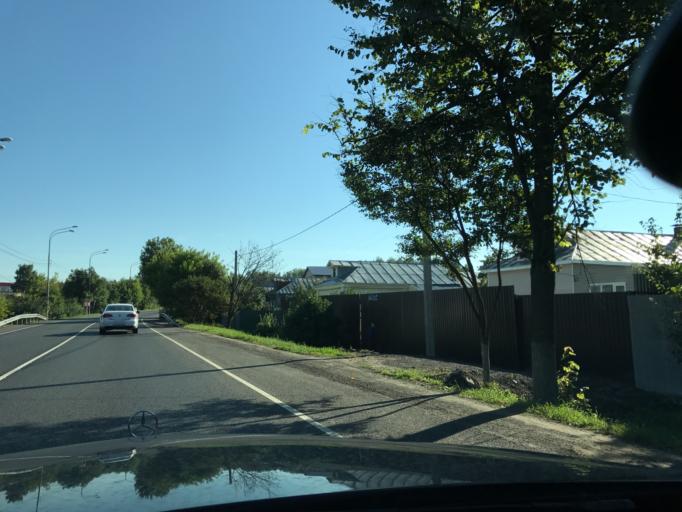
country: RU
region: Moskovskaya
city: Sverdlovskiy
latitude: 55.9248
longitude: 38.1348
